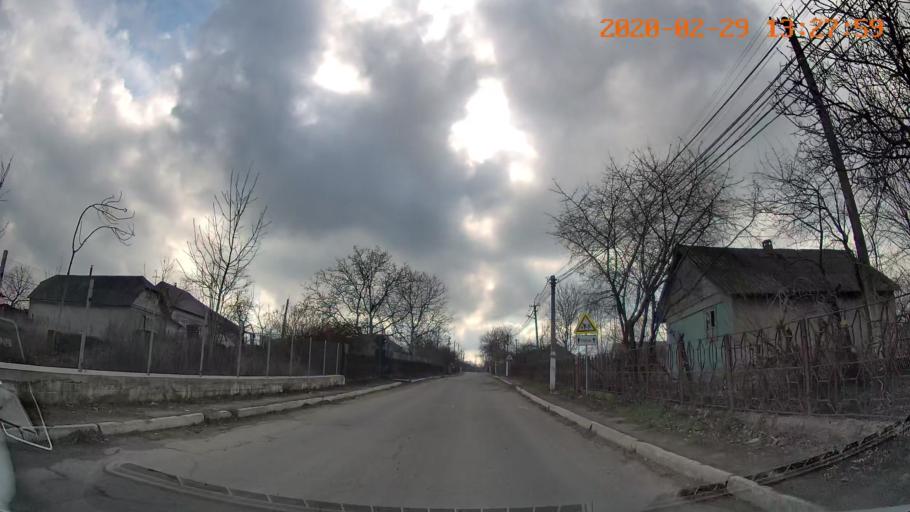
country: MD
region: Telenesti
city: Camenca
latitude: 47.9089
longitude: 28.6445
